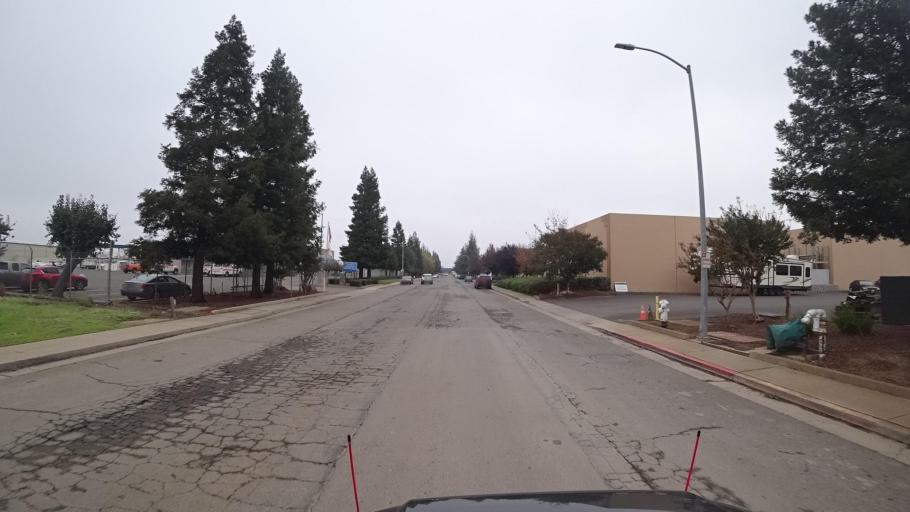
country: US
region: California
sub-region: Sacramento County
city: Elk Grove
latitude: 38.3826
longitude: -121.3636
